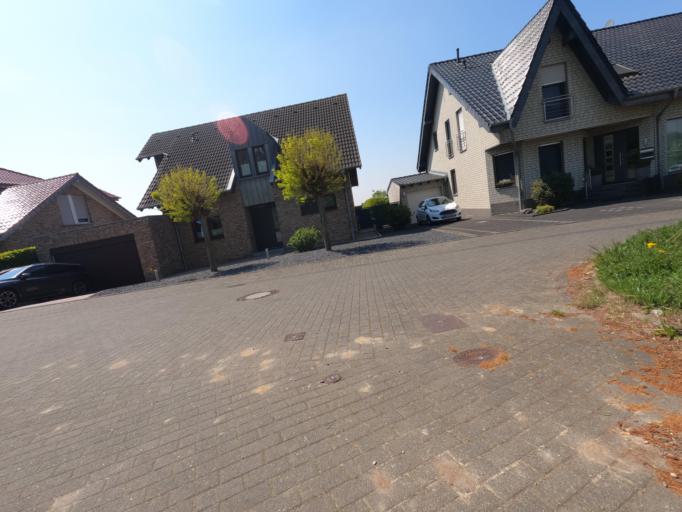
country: DE
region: North Rhine-Westphalia
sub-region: Regierungsbezirk Koln
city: Ubach-Palenberg
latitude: 50.9075
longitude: 6.1345
